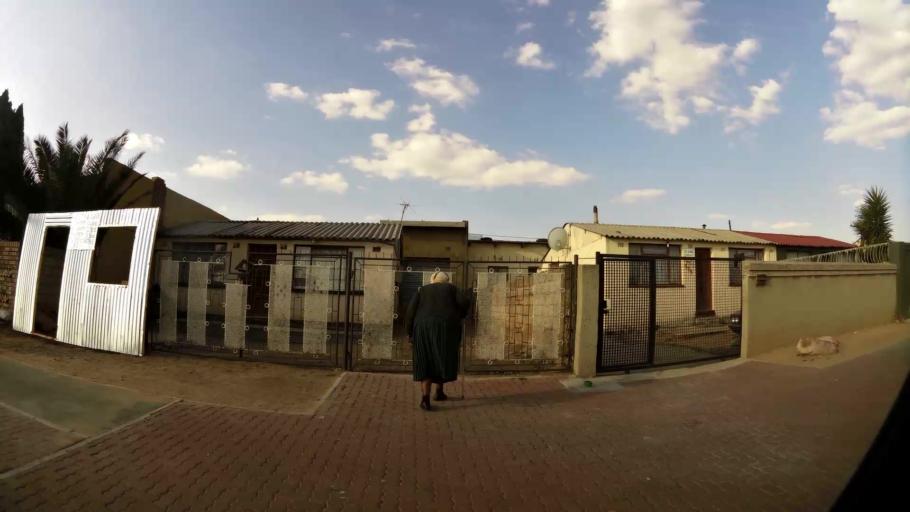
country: ZA
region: Gauteng
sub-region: City of Johannesburg Metropolitan Municipality
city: Soweto
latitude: -26.2235
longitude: 27.8916
